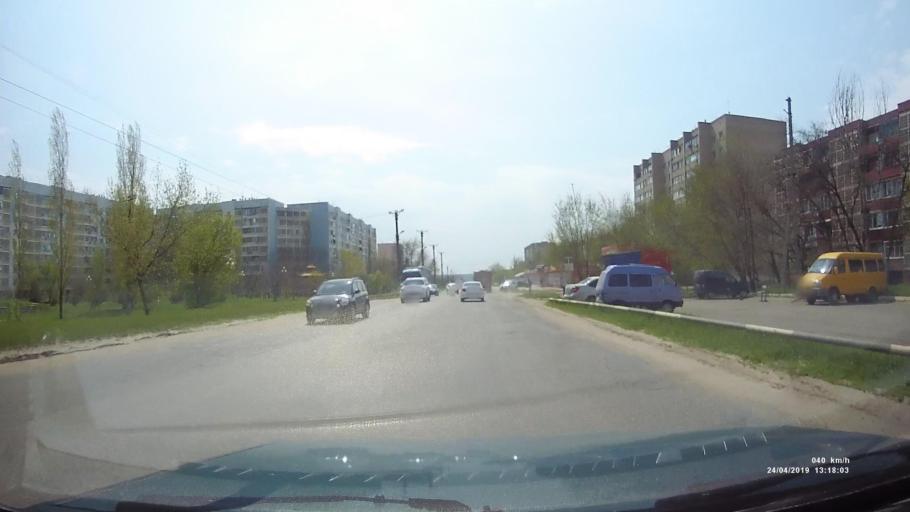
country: RU
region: Kalmykiya
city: Elista
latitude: 46.3041
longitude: 44.2966
